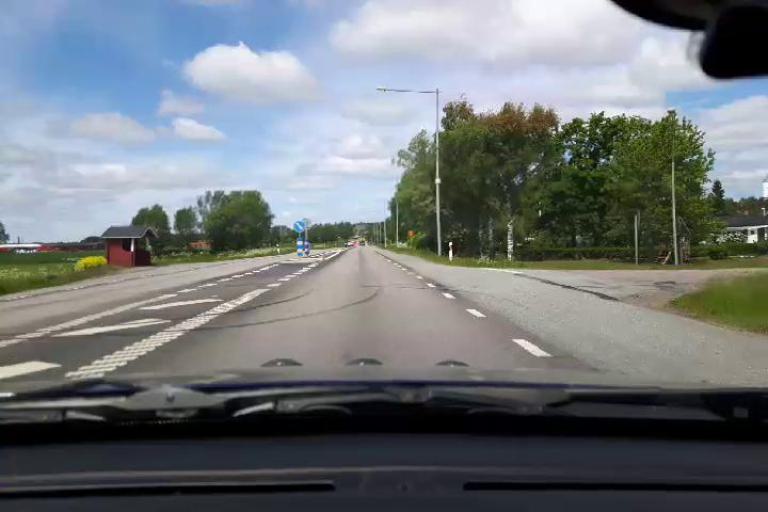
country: SE
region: Uppsala
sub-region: Osthammars Kommun
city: Bjorklinge
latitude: 60.0192
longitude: 17.5560
